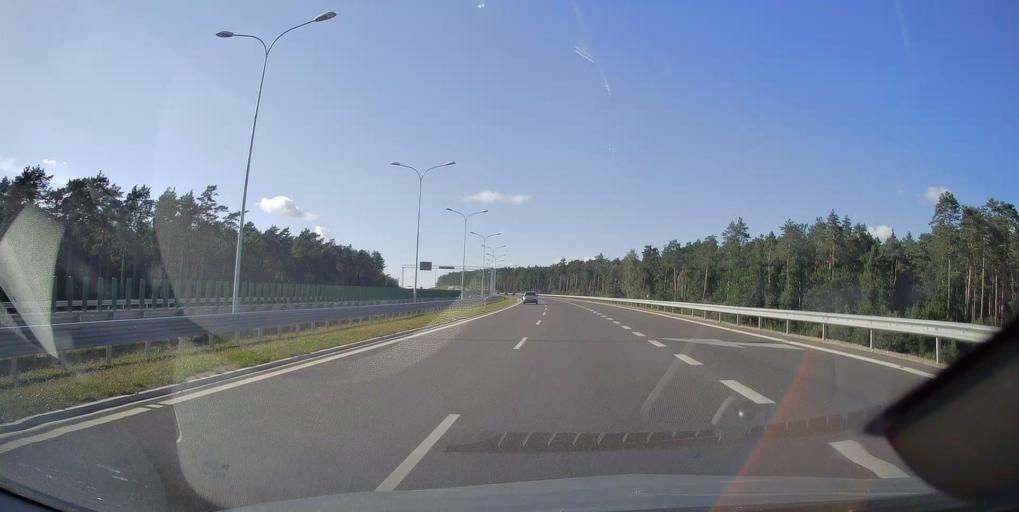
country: PL
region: Swietokrzyskie
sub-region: Powiat skarzyski
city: Skarzysko-Kamienna
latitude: 51.1216
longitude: 20.8466
